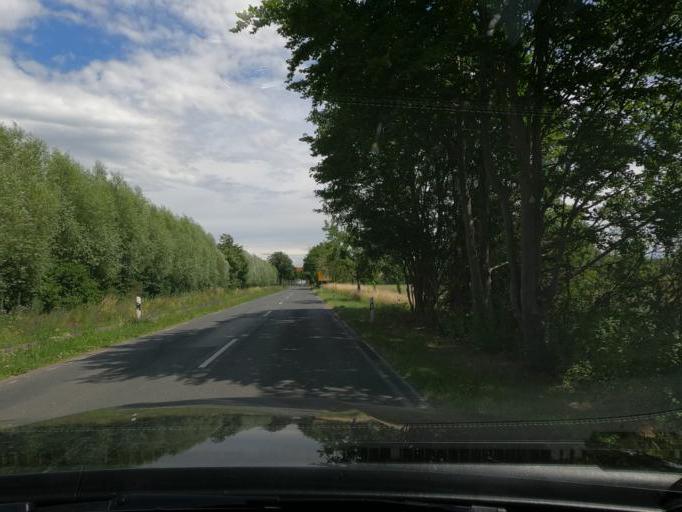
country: DE
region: Lower Saxony
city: Lengede
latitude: 52.1909
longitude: 10.3187
